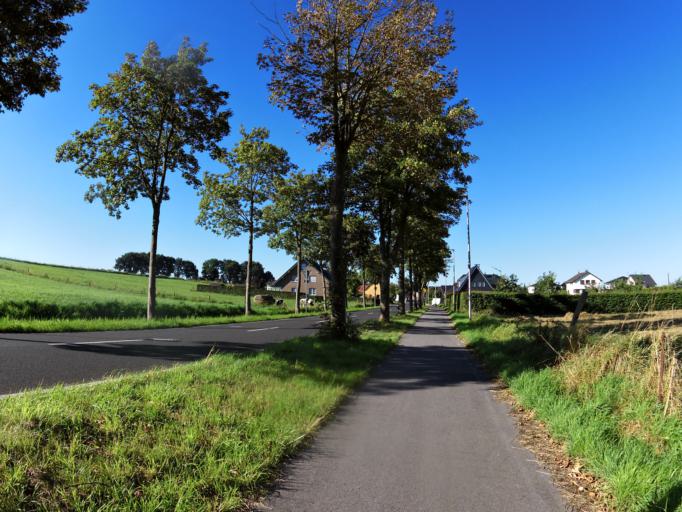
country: DE
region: North Rhine-Westphalia
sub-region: Regierungsbezirk Koln
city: Ubach-Palenberg
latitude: 50.9484
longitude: 6.0748
